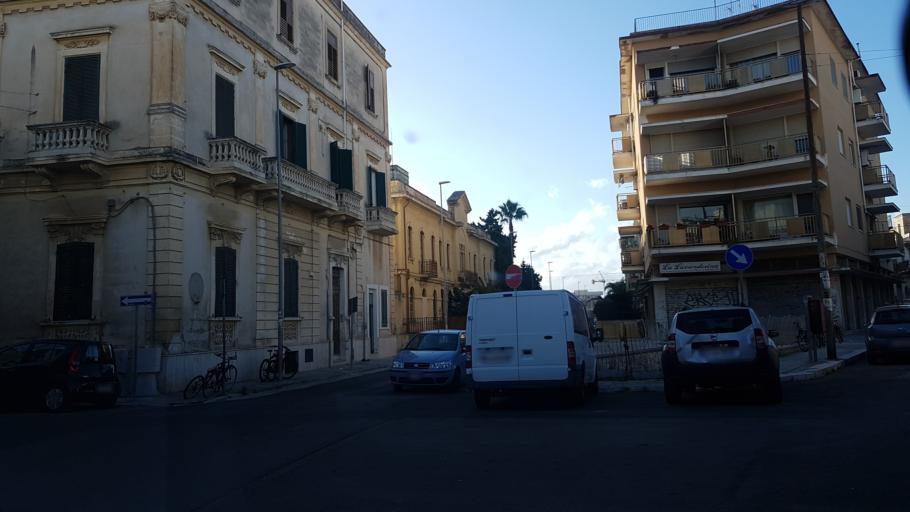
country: IT
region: Apulia
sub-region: Provincia di Lecce
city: Lecce
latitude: 40.3521
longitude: 18.1597
